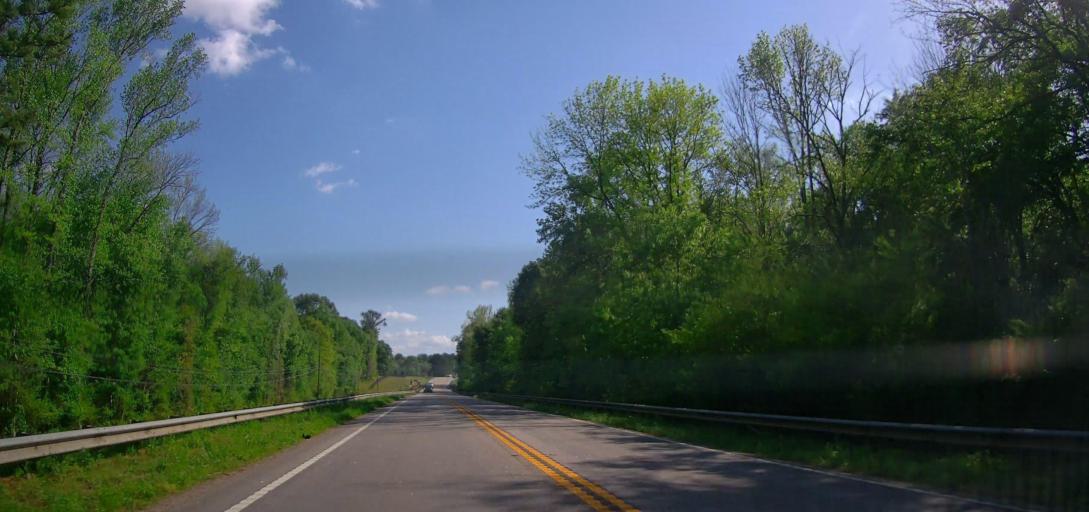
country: US
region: Georgia
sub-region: Morgan County
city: Madison
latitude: 33.6460
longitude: -83.4478
